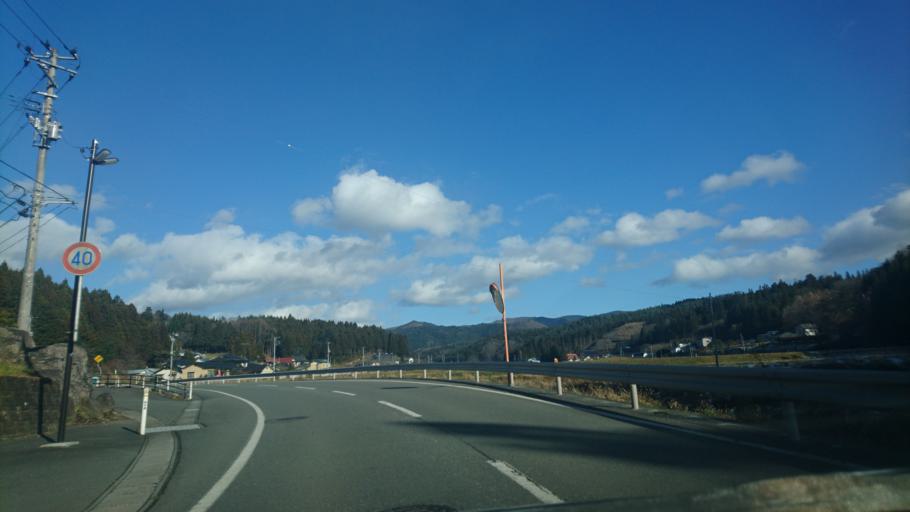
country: JP
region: Iwate
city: Mizusawa
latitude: 39.0568
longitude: 141.3663
